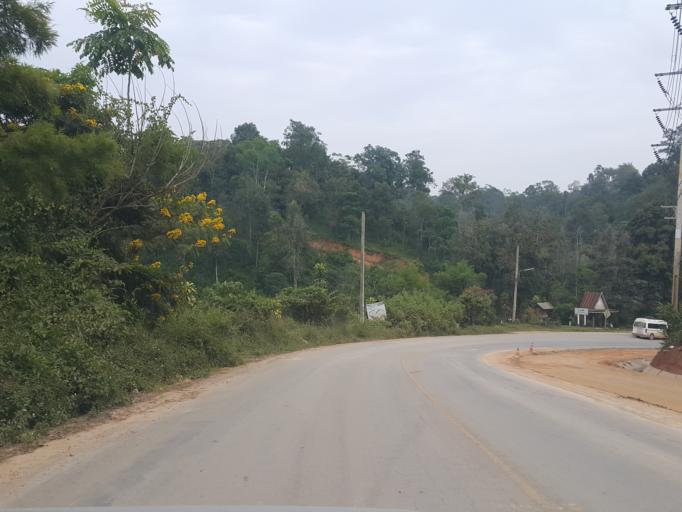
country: TH
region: Chiang Mai
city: Mae Taeng
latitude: 19.1194
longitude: 98.7182
